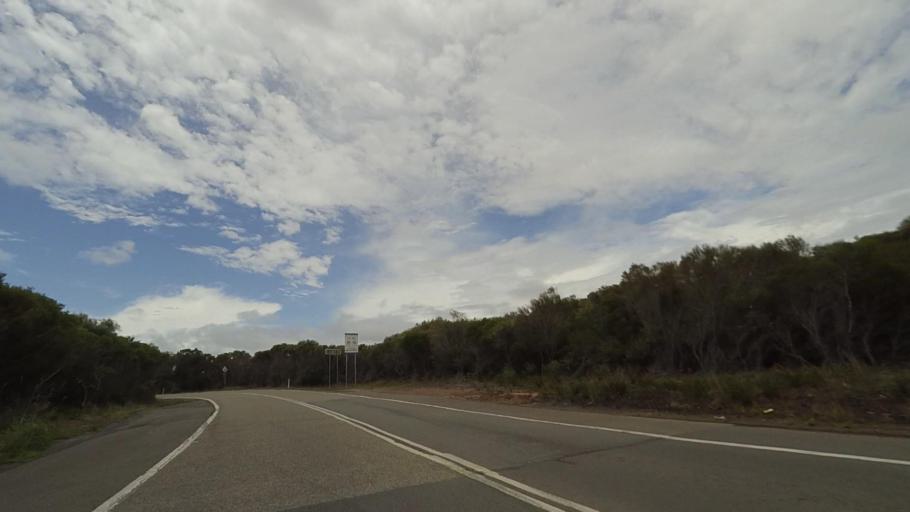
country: AU
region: New South Wales
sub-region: Sutherland Shire
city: Grays Point
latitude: -34.1301
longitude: 151.0811
